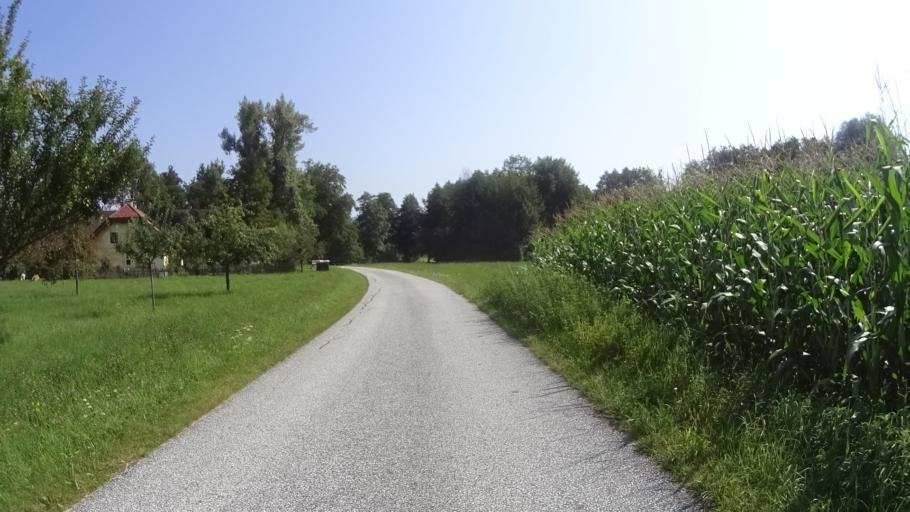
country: AT
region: Carinthia
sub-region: Politischer Bezirk Volkermarkt
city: Gallizien
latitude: 46.5611
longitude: 14.4937
